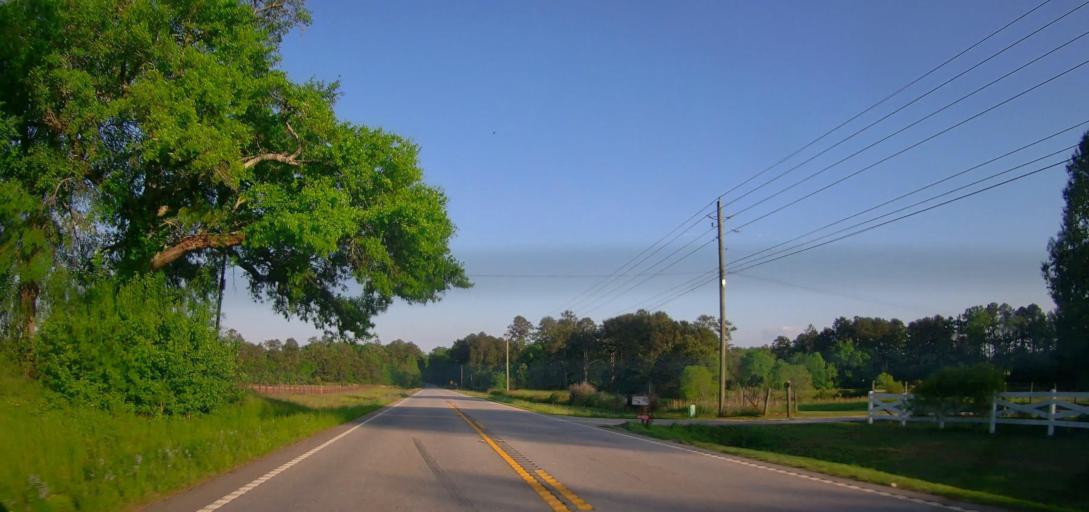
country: US
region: Georgia
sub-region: Walton County
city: Social Circle
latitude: 33.5589
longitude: -83.7486
